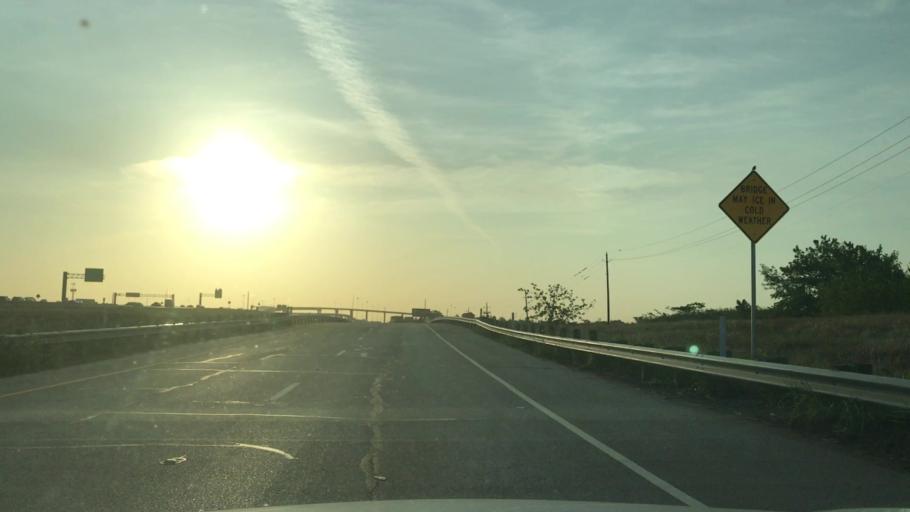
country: US
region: Texas
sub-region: Dallas County
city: Farmers Branch
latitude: 32.9058
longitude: -96.9164
